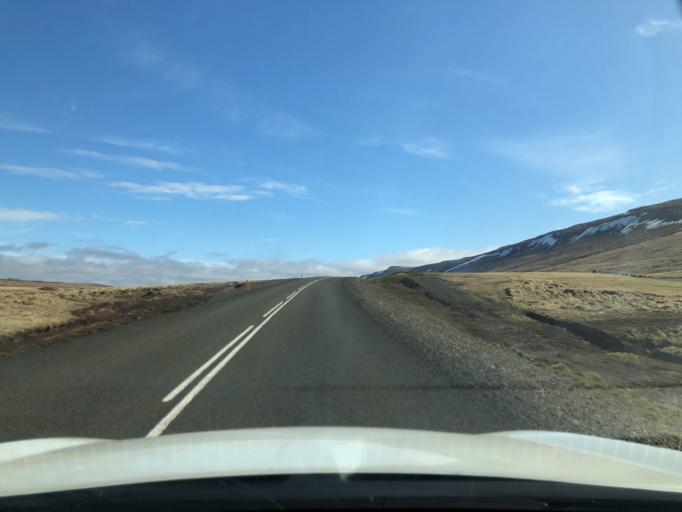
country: IS
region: West
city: Borgarnes
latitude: 65.1465
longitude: -21.5859
